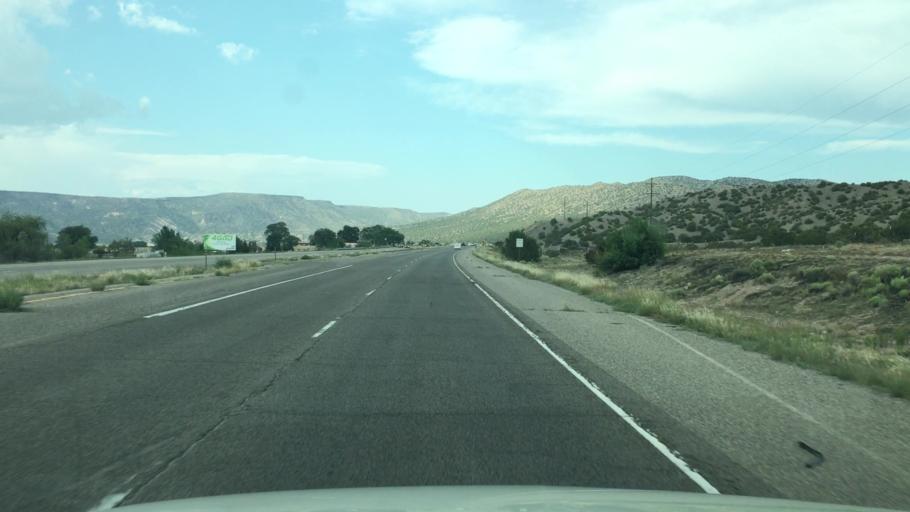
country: US
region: New Mexico
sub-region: Rio Arriba County
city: Ohkay Owingeh
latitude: 36.1413
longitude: -105.9886
